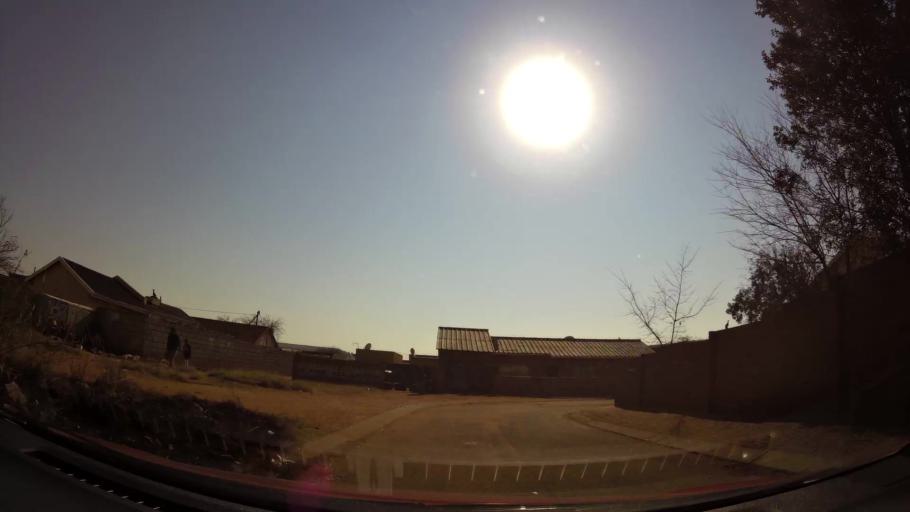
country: ZA
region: Gauteng
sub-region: City of Johannesburg Metropolitan Municipality
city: Johannesburg
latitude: -26.2455
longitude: 27.9567
